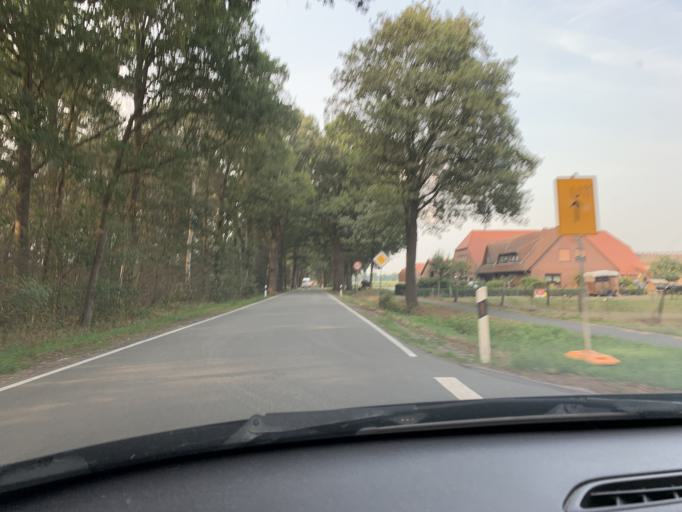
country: DE
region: Lower Saxony
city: Apen
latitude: 53.2000
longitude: 7.7930
